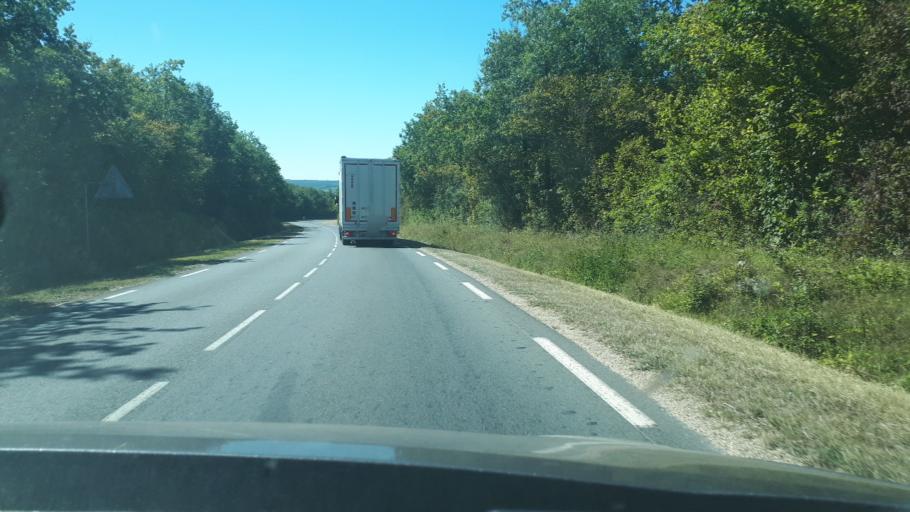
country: FR
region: Centre
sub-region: Departement du Cher
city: Sancerre
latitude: 47.3109
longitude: 2.8082
